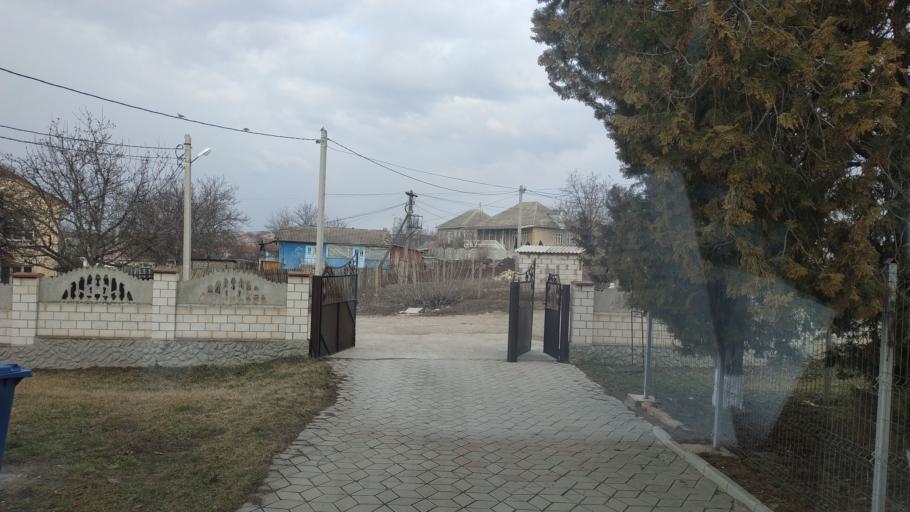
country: MD
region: Chisinau
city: Singera
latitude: 46.9658
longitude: 29.0559
